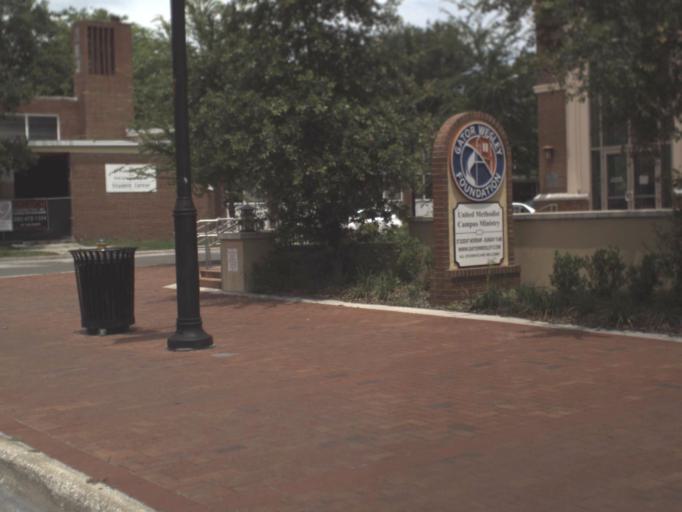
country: US
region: Florida
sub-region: Alachua County
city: Gainesville
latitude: 29.6521
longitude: -82.3402
